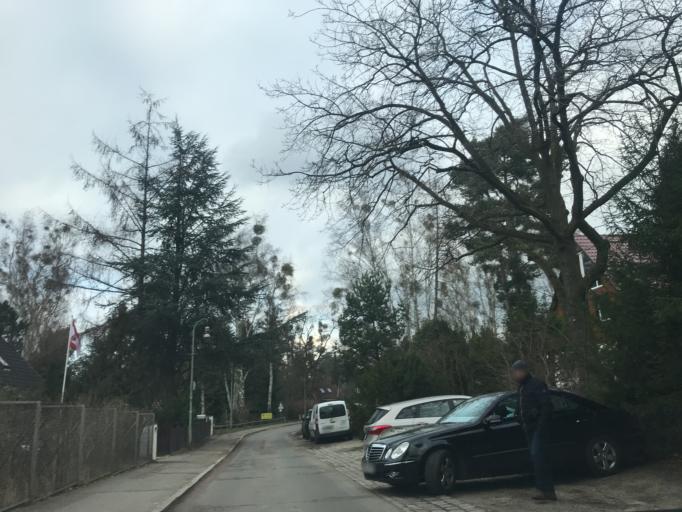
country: DE
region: Berlin
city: Kladow
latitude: 52.4518
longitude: 13.1305
